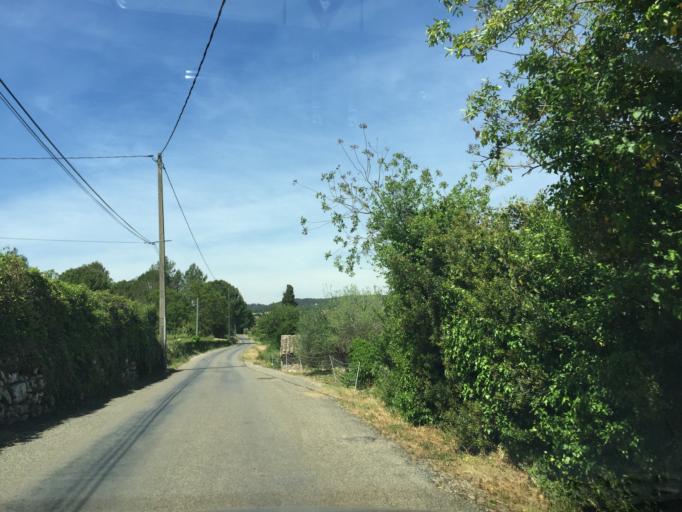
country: FR
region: Provence-Alpes-Cote d'Azur
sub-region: Departement du Var
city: Lorgues
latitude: 43.4815
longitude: 6.3660
